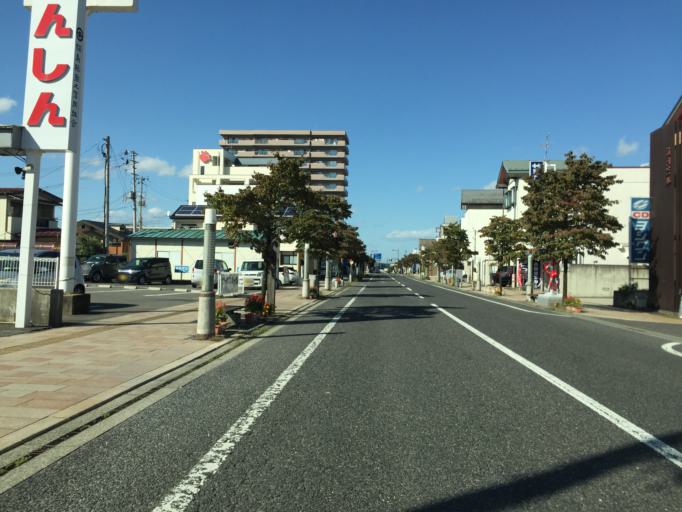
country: JP
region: Fukushima
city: Sukagawa
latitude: 37.2910
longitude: 140.3759
